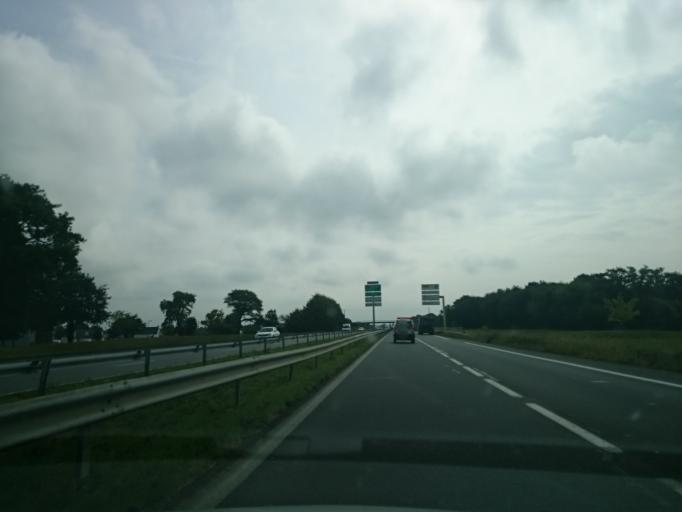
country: FR
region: Brittany
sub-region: Departement du Morbihan
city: Peaule
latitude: 47.5363
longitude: -2.4021
